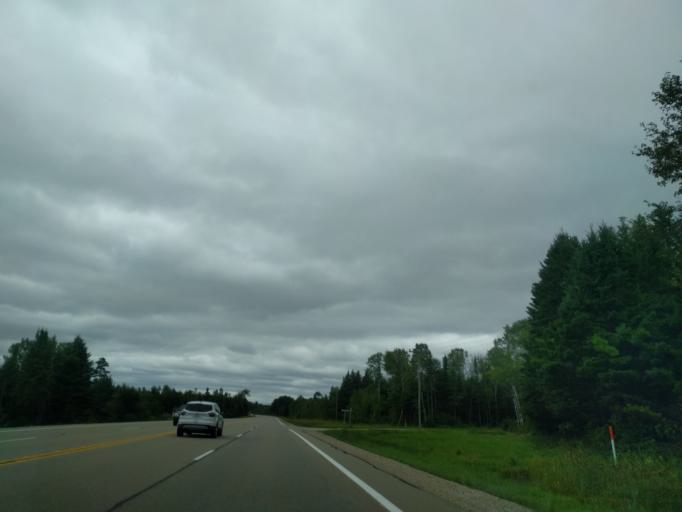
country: US
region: Michigan
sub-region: Delta County
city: Escanaba
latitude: 45.5379
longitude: -87.2818
